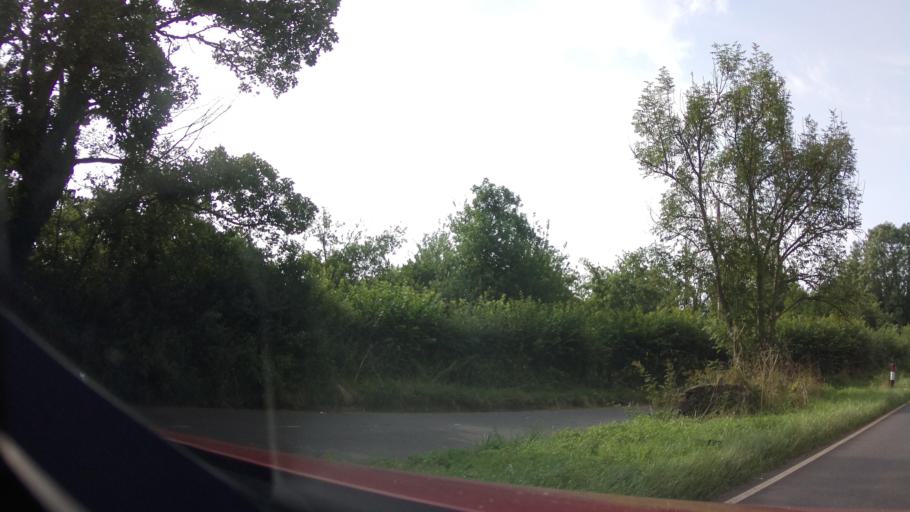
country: GB
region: England
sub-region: Bath and North East Somerset
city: Chew Magna
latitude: 51.3443
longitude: -2.6338
